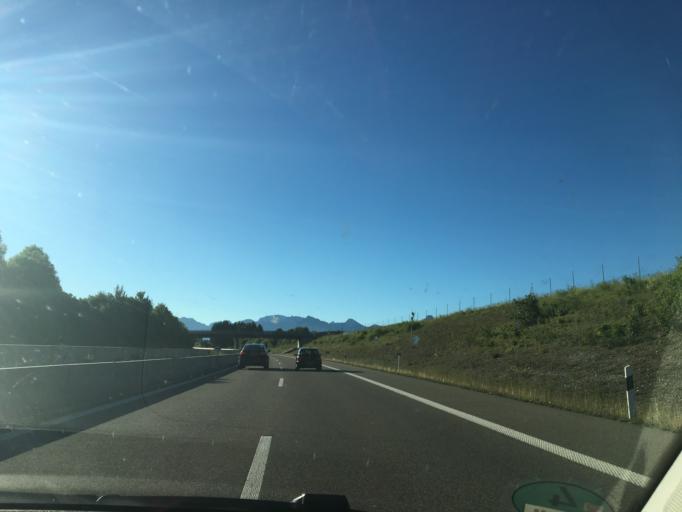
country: DE
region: Bavaria
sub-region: Swabia
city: Seeg
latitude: 47.6297
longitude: 10.5758
